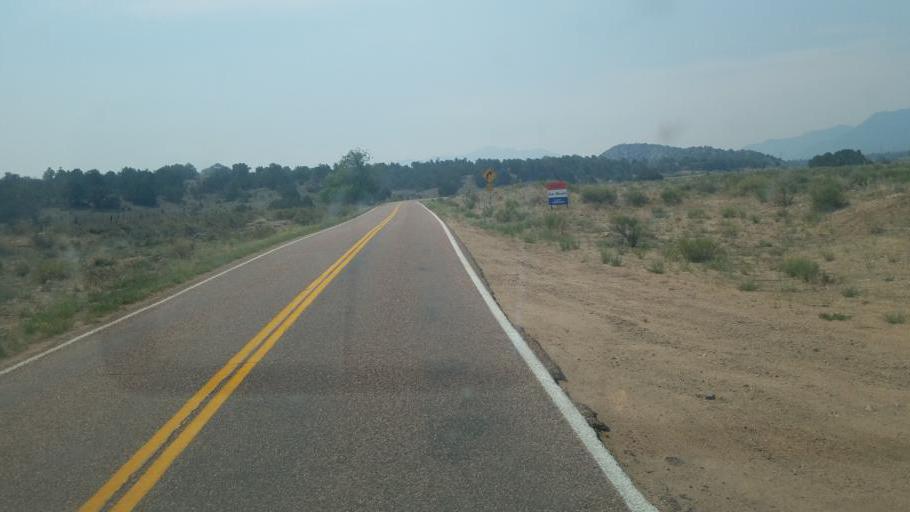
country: US
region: Colorado
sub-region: Fremont County
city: Canon City
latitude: 38.4564
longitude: -105.3742
